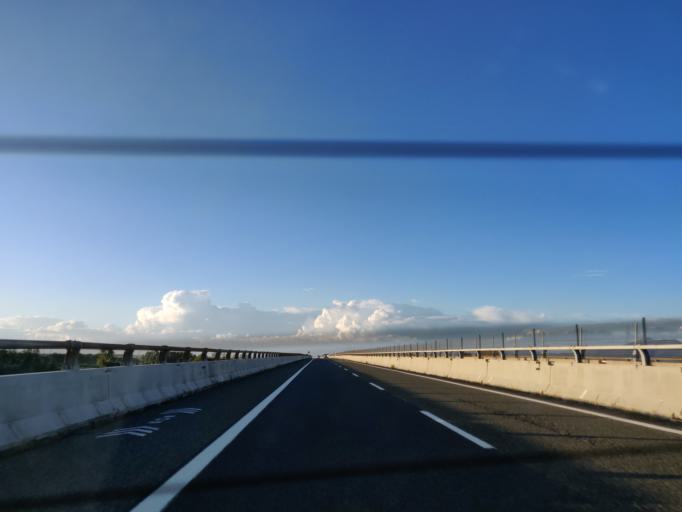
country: IT
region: Tuscany
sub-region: Provincia di Livorno
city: Vicarello
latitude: 43.5987
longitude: 10.4499
